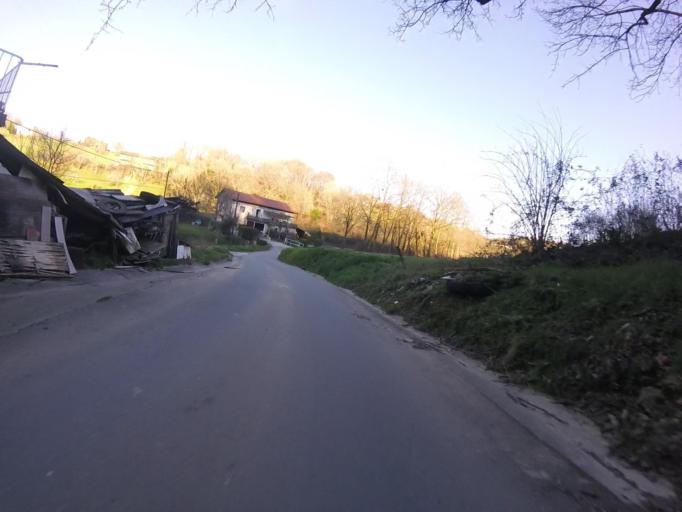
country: ES
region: Basque Country
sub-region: Provincia de Guipuzcoa
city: Errenteria
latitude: 43.2904
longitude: -1.8765
